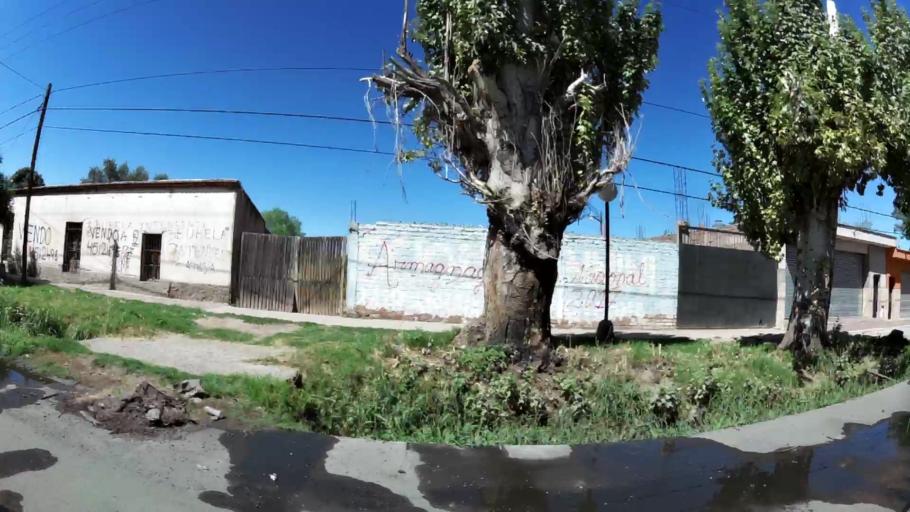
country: AR
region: Mendoza
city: Las Heras
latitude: -32.8374
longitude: -68.8335
